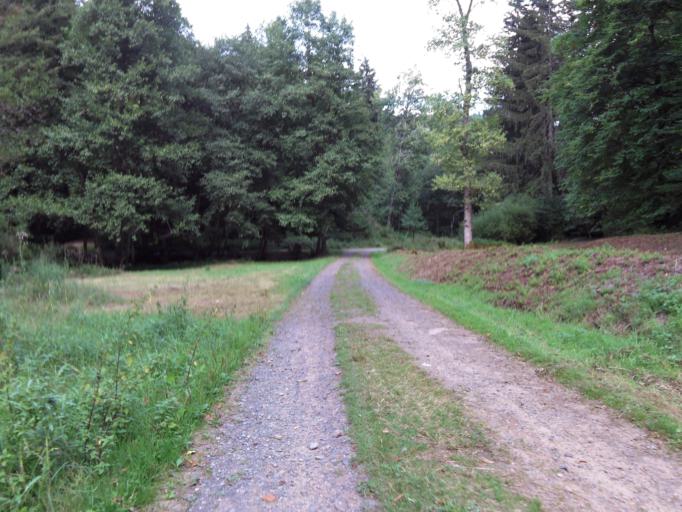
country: DE
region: Rheinland-Pfalz
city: Carlsberg
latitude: 49.4603
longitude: 8.0247
